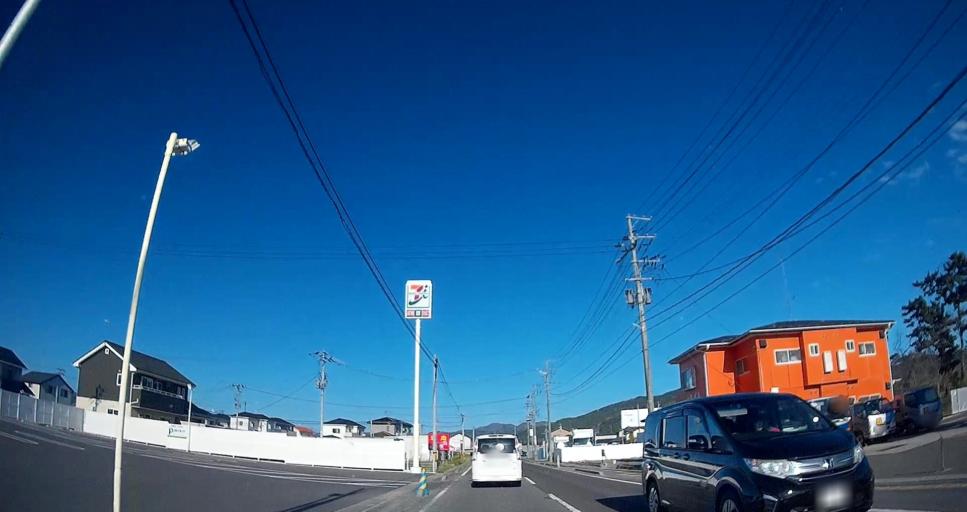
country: JP
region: Miyagi
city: Ishinomaki
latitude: 38.4168
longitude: 141.3550
